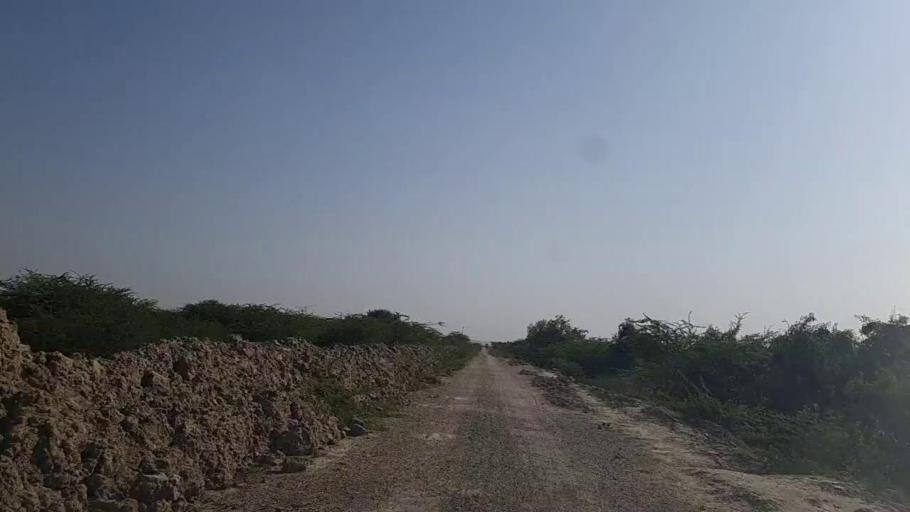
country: PK
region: Sindh
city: Kadhan
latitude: 24.5827
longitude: 69.2629
